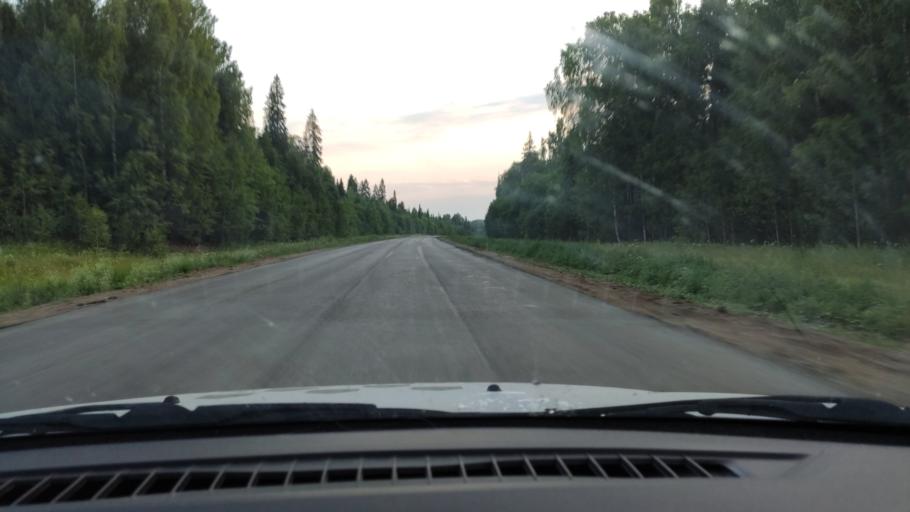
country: RU
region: Perm
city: Siva
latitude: 58.4681
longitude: 54.4065
